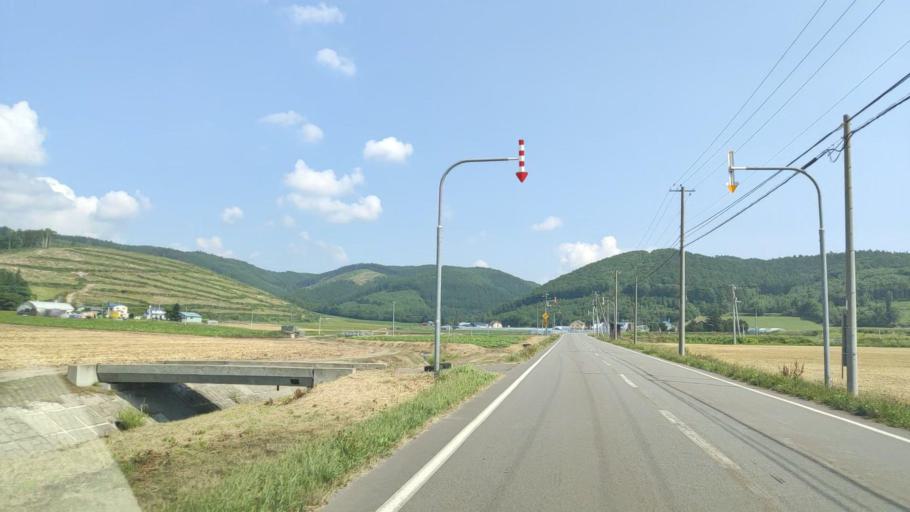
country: JP
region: Hokkaido
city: Shimo-furano
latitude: 43.4142
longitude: 142.3992
